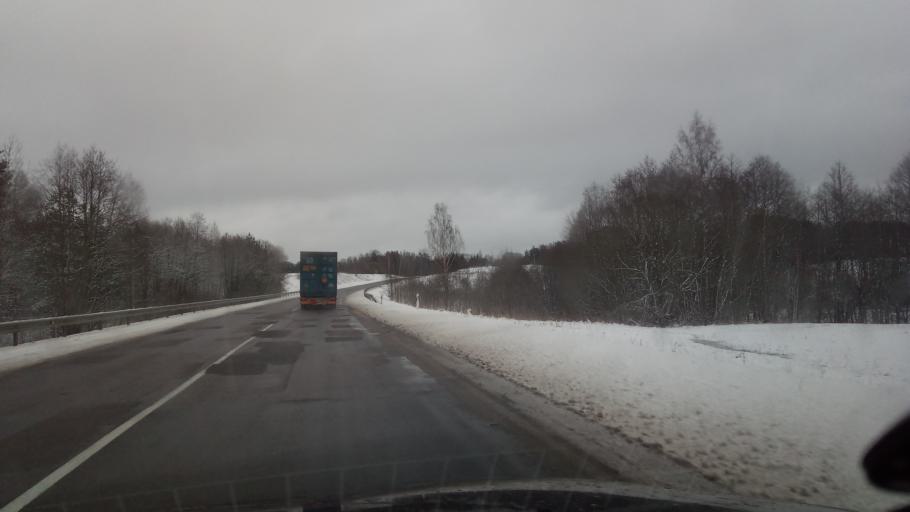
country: LT
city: Zarasai
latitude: 55.6344
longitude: 25.9695
